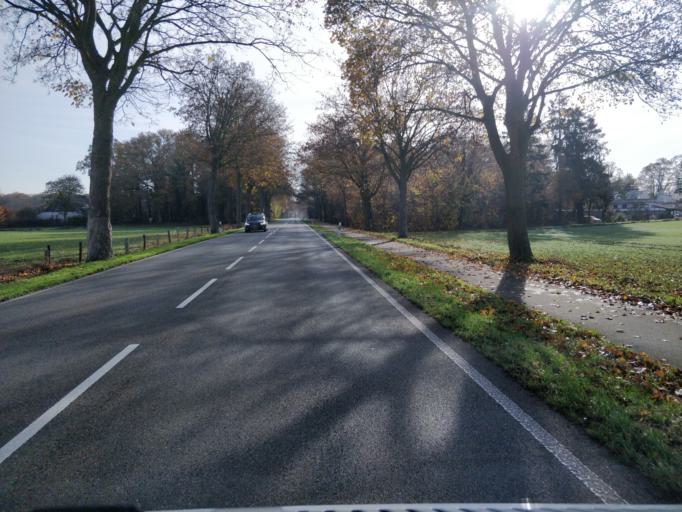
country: DE
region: North Rhine-Westphalia
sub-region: Regierungsbezirk Dusseldorf
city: Mehrhoog
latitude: 51.7244
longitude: 6.5096
